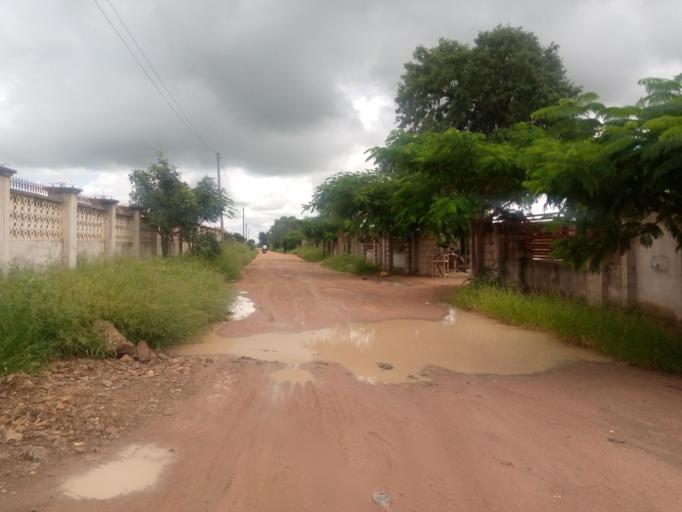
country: TZ
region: Dodoma
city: Dodoma
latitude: -6.1229
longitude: 35.7397
